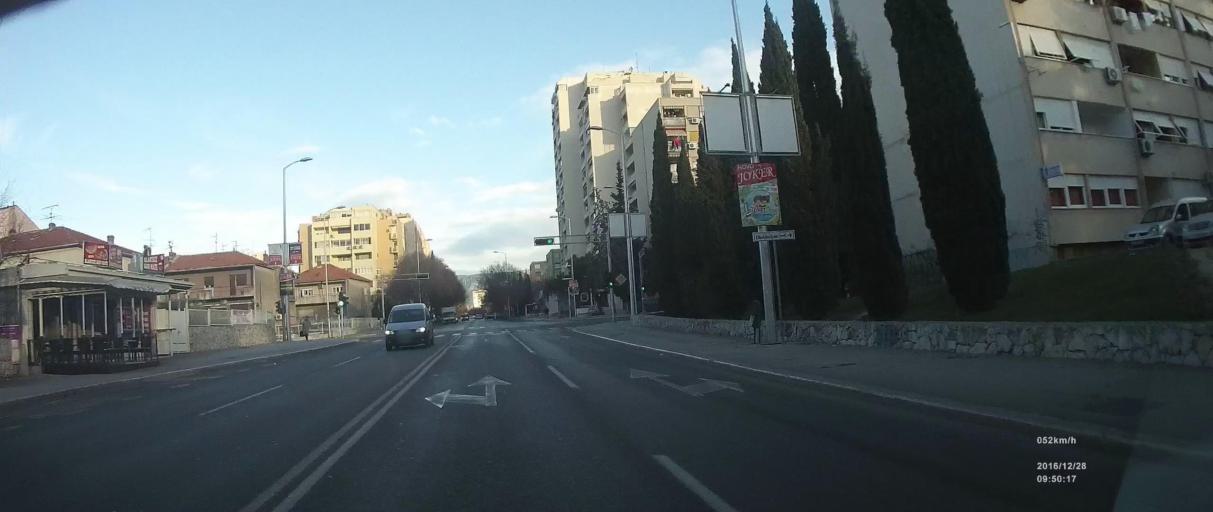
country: HR
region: Splitsko-Dalmatinska
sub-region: Grad Split
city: Split
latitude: 43.5086
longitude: 16.4554
